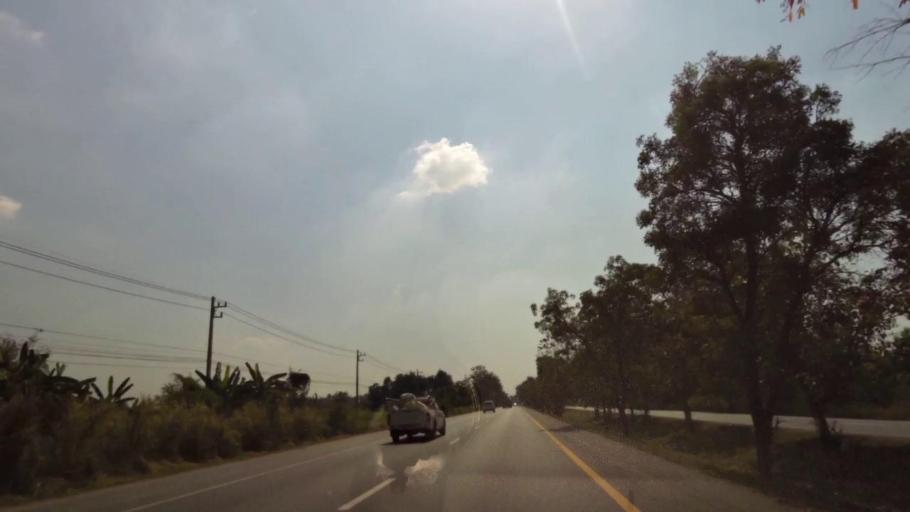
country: TH
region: Phichit
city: Bueng Na Rang
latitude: 16.1665
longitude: 100.1266
